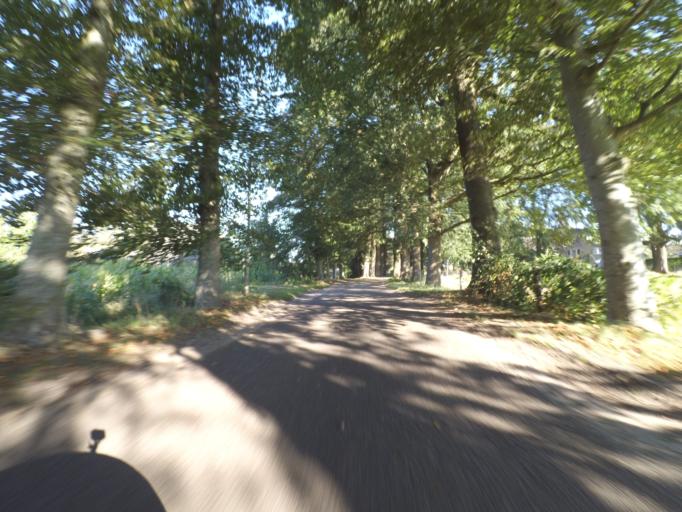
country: NL
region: Gelderland
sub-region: Gemeente Barneveld
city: Voorthuizen
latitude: 52.1799
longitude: 5.5606
